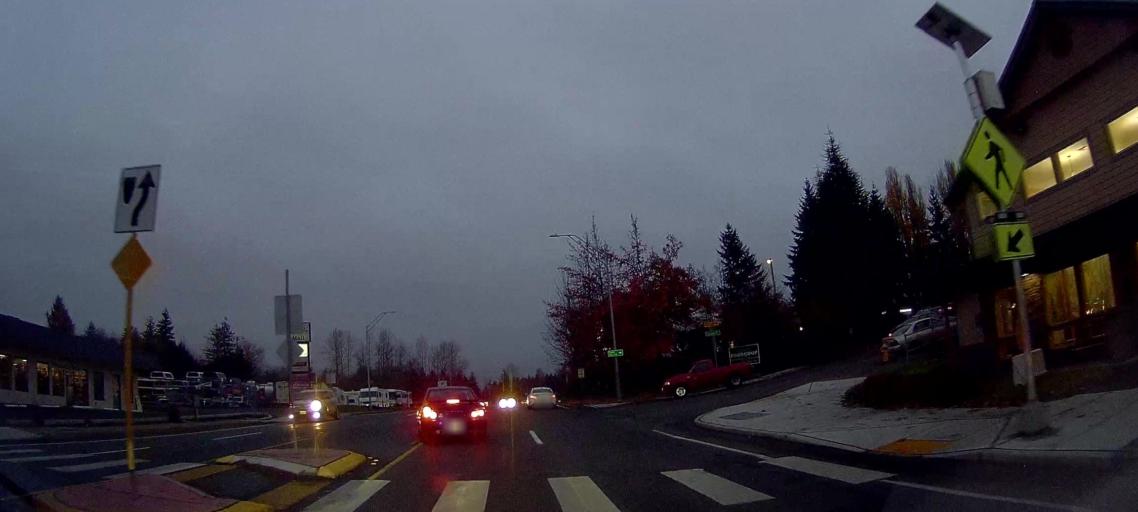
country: US
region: Washington
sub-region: Thurston County
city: Lacey
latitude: 47.0426
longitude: -122.8572
